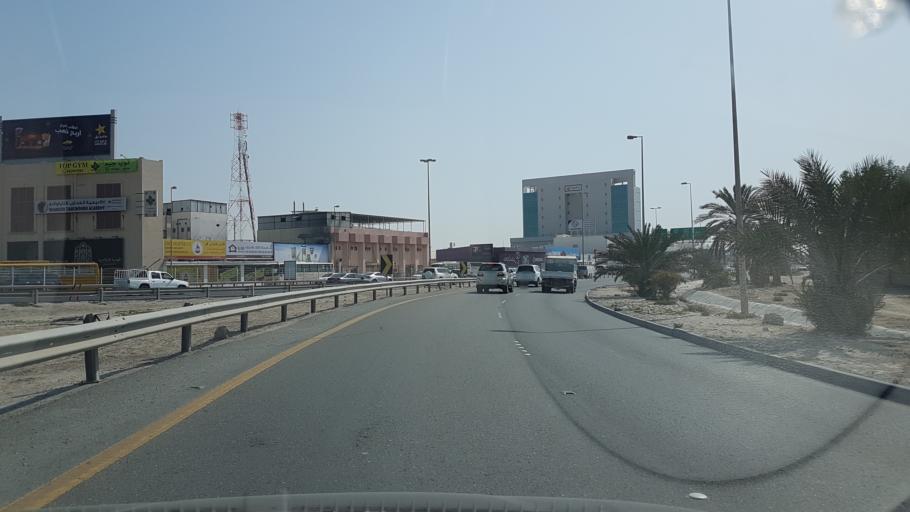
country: BH
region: Northern
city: Madinat `Isa
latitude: 26.1927
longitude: 50.5347
